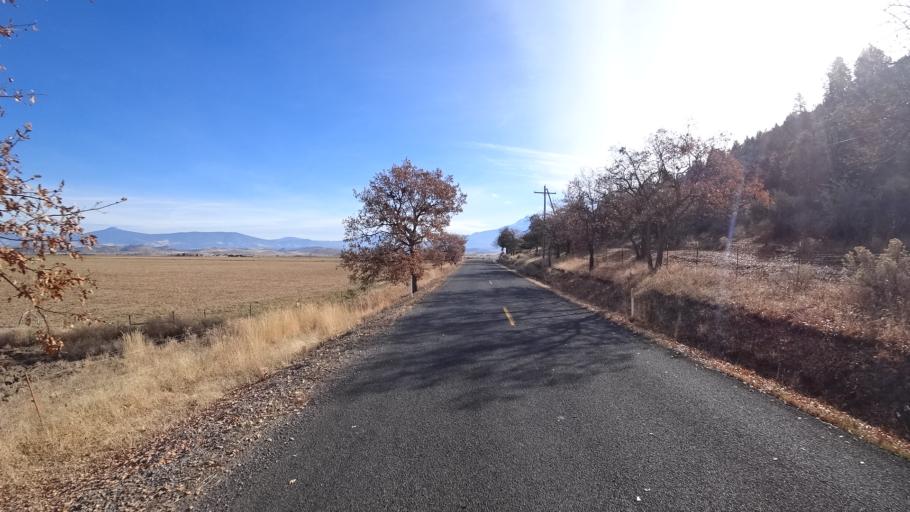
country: US
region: California
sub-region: Siskiyou County
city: Montague
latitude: 41.5390
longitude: -122.5667
